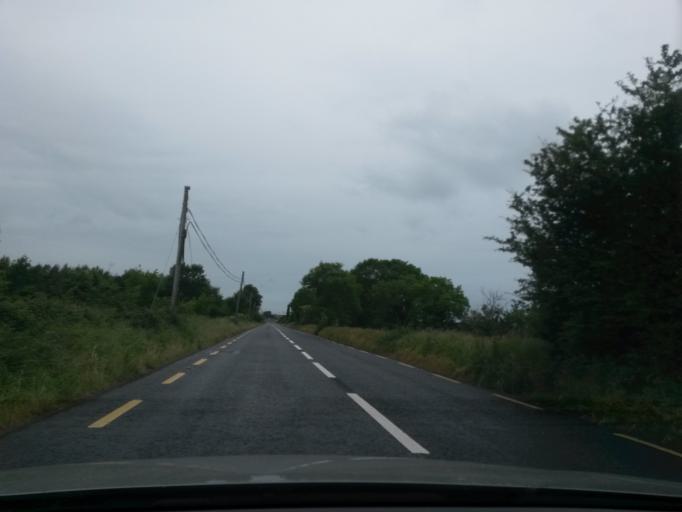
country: IE
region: Connaught
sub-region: Sligo
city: Strandhill
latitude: 54.2444
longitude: -8.7085
